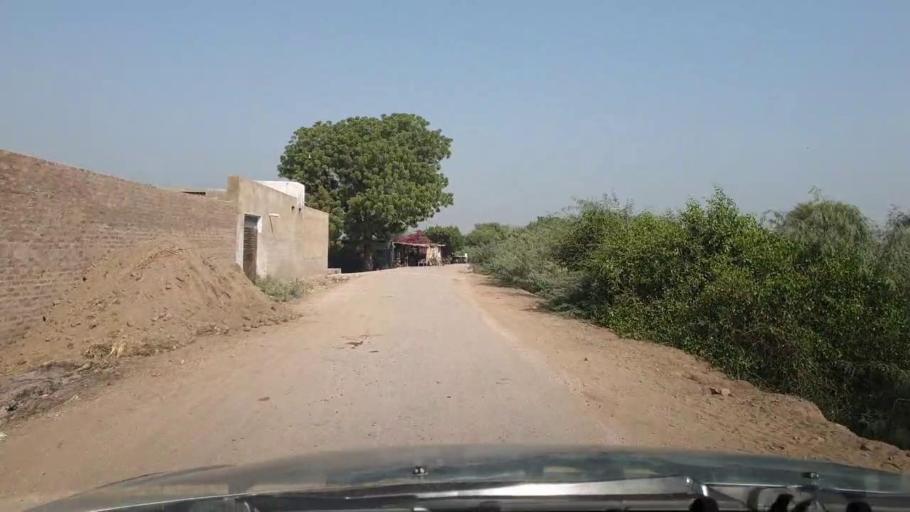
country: PK
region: Sindh
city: Tando Jam
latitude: 25.3112
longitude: 68.5394
